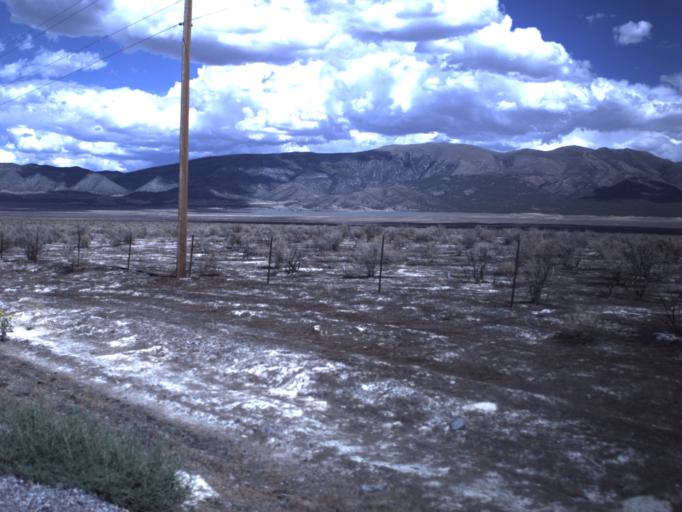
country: US
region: Utah
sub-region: Tooele County
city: Grantsville
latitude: 40.2521
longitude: -112.7015
